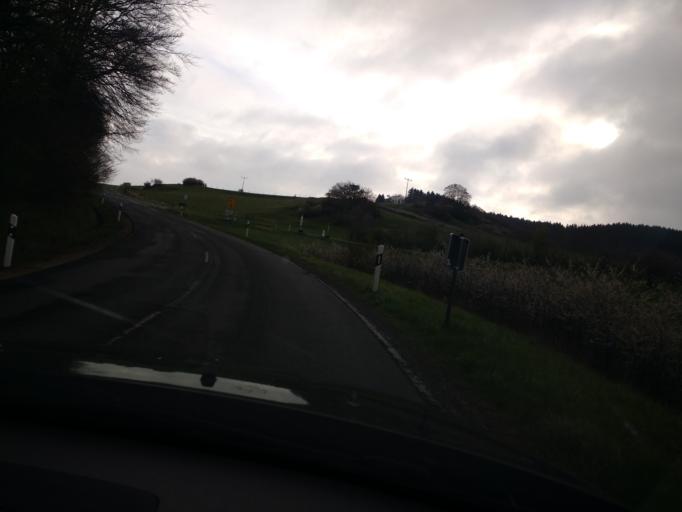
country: DE
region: Rheinland-Pfalz
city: Kalenborn-Scheuern
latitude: 50.2469
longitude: 6.5851
